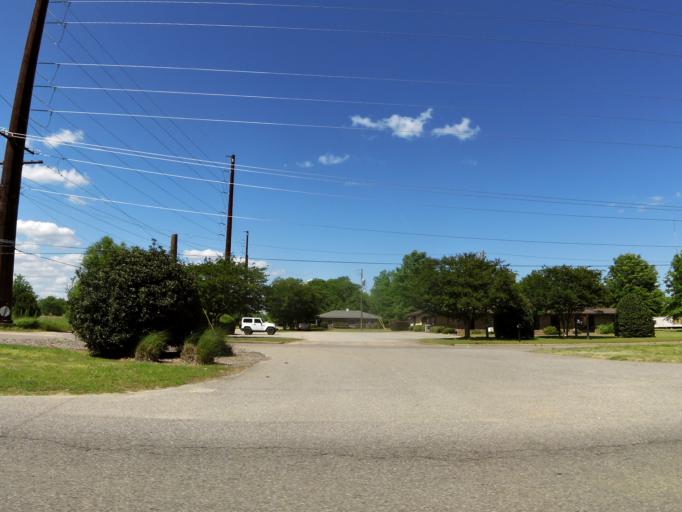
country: US
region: South Carolina
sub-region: Aiken County
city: Aiken
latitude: 33.5550
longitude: -81.7027
